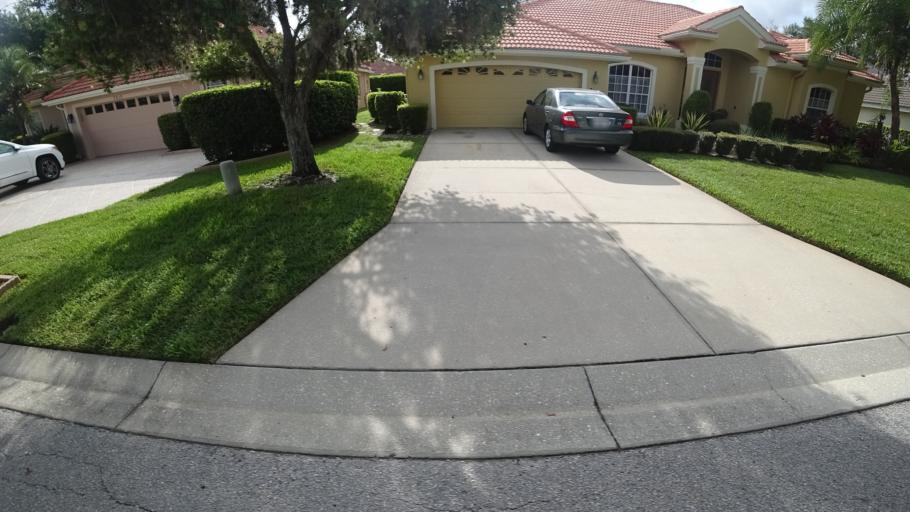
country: US
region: Florida
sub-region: Sarasota County
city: Desoto Lakes
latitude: 27.4116
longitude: -82.4846
